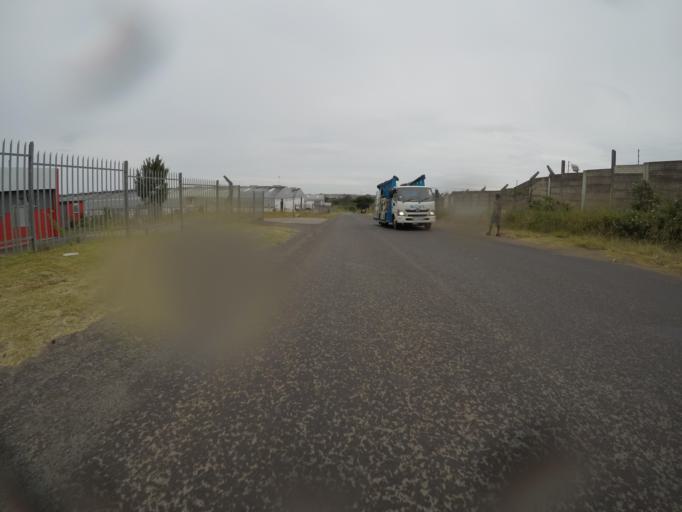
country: ZA
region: Eastern Cape
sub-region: Buffalo City Metropolitan Municipality
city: East London
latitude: -32.9792
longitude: 27.8234
